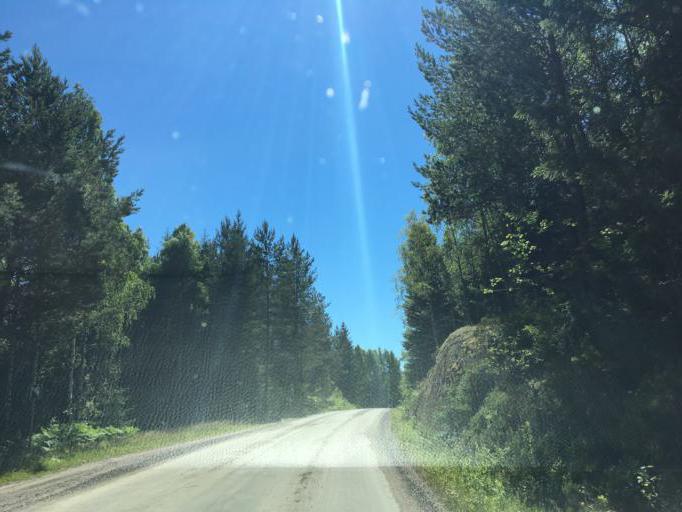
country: SE
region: Vaestra Goetaland
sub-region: Karlsborgs Kommun
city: Karlsborg
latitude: 58.7317
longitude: 14.5911
